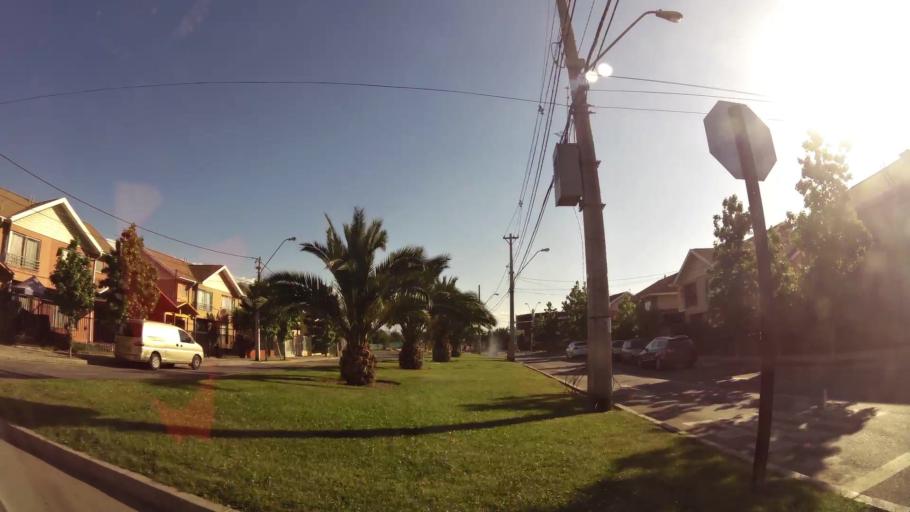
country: CL
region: Santiago Metropolitan
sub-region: Provincia de Maipo
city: San Bernardo
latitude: -33.5517
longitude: -70.7635
